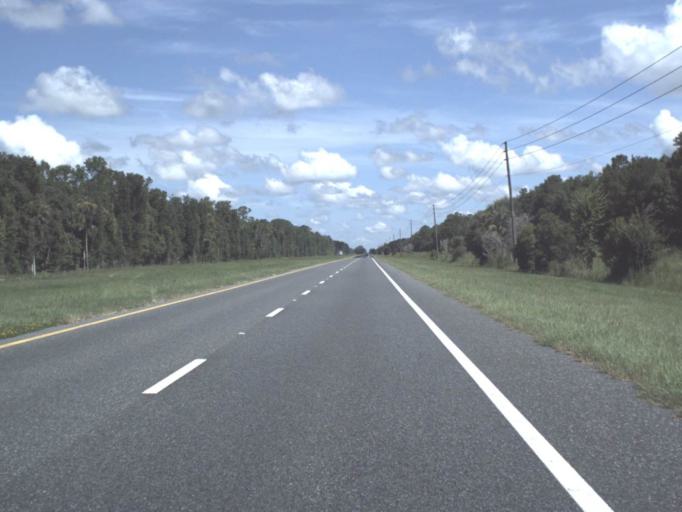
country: US
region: Florida
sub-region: Levy County
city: Inglis
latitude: 29.2242
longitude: -82.7054
